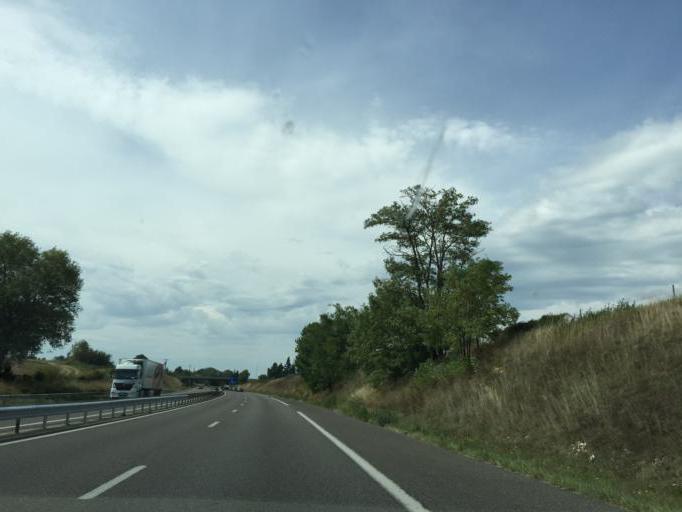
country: FR
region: Rhone-Alpes
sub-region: Departement de l'Isere
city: Cessieu
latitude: 45.5613
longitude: 5.3828
